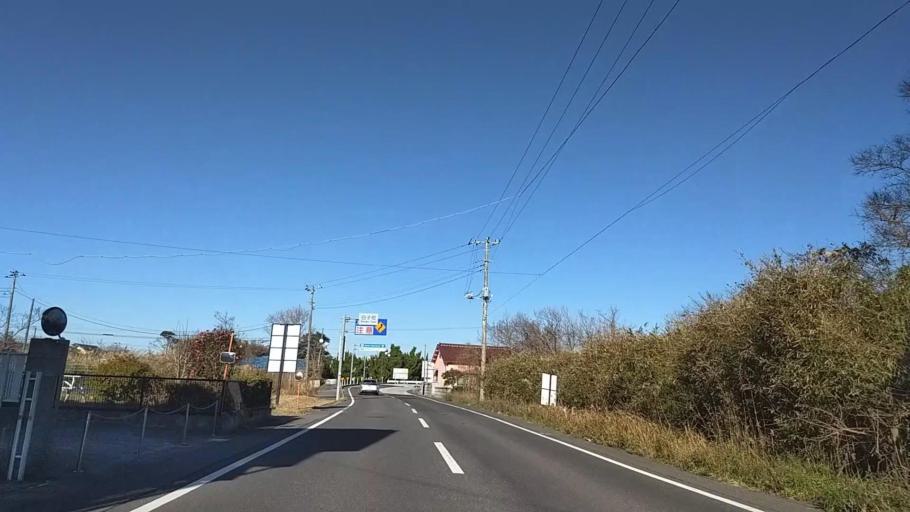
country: JP
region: Chiba
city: Mobara
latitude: 35.4190
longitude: 140.3919
